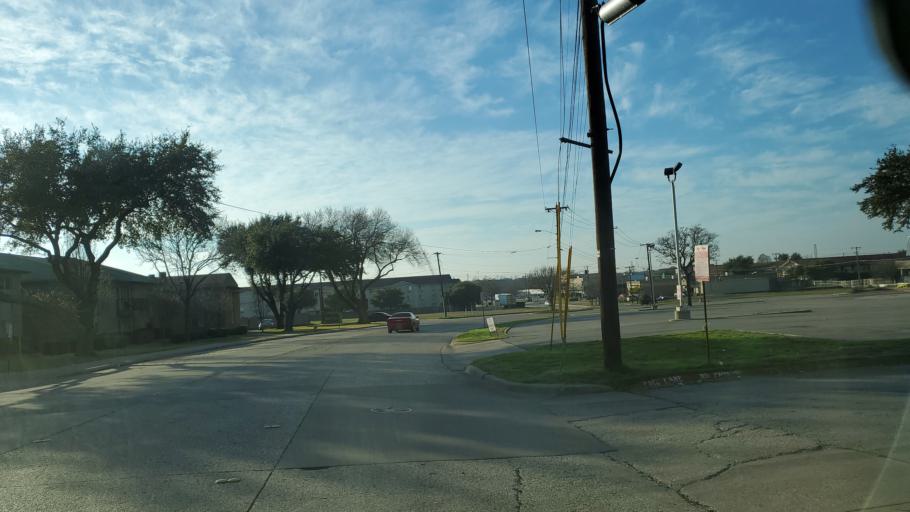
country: US
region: Texas
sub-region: Collin County
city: Plano
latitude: 33.0241
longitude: -96.7060
